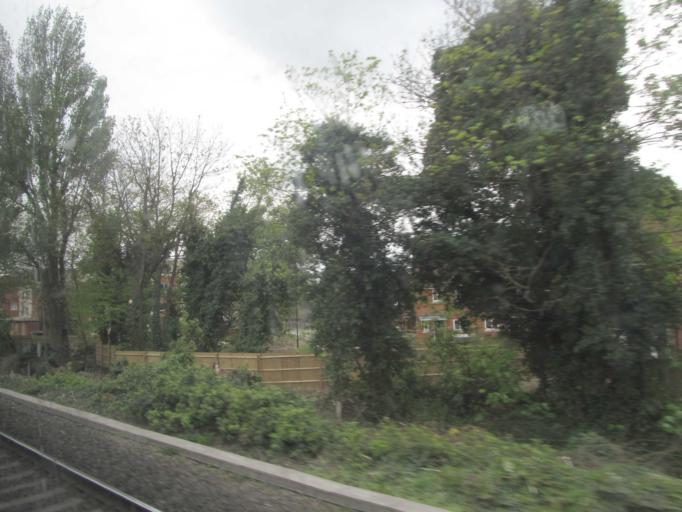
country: GB
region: England
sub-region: Slough
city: Slough
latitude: 51.5101
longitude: -0.5768
